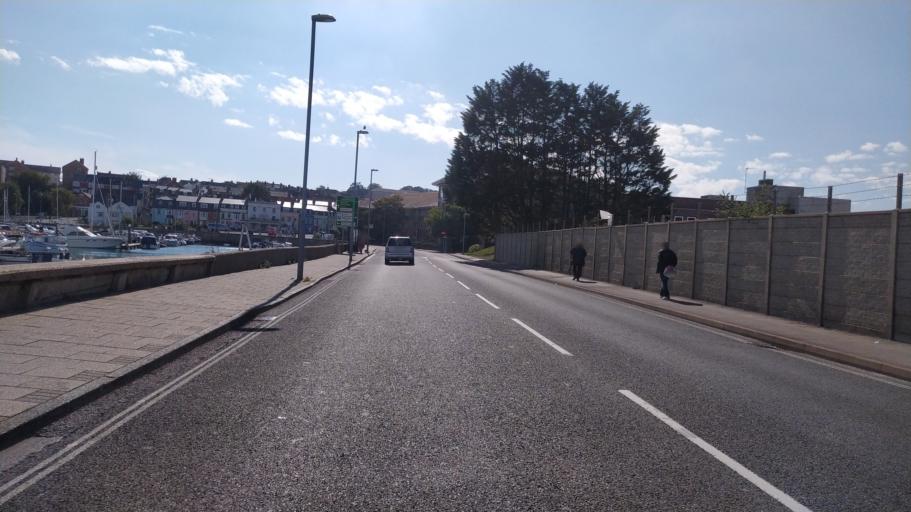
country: GB
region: England
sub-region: Dorset
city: Weymouth
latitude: 50.6091
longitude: -2.4594
